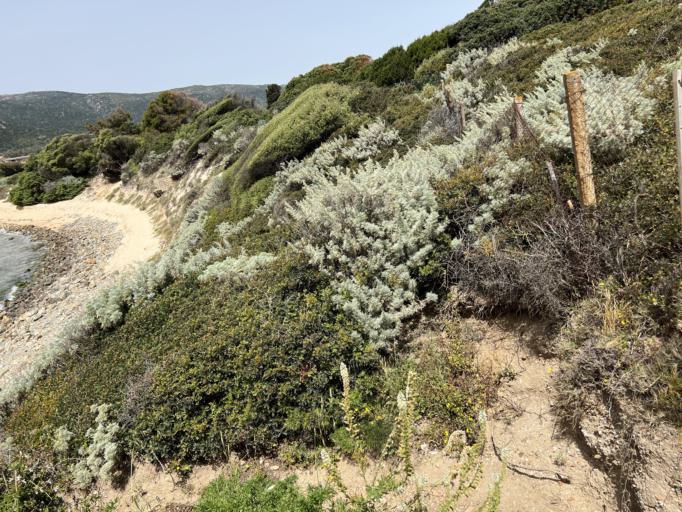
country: IT
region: Sardinia
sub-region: Provincia di Cagliari
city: Domus de Maria
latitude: 38.8959
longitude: 8.8837
